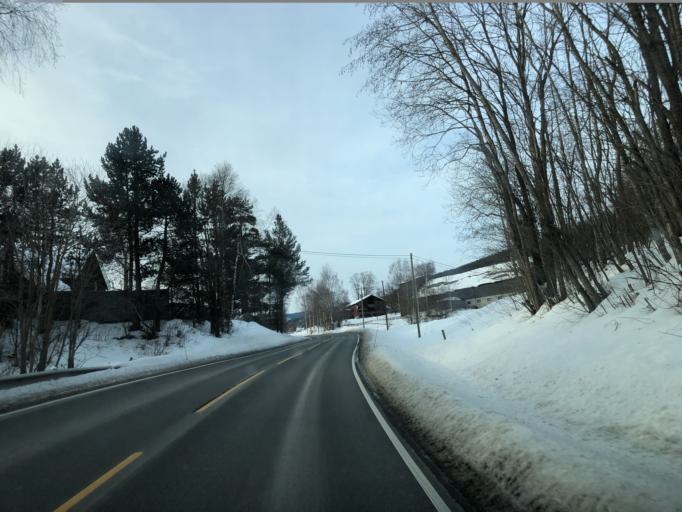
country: NO
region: Oppland
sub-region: Gausdal
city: Segalstad bru
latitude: 61.2386
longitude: 10.2022
